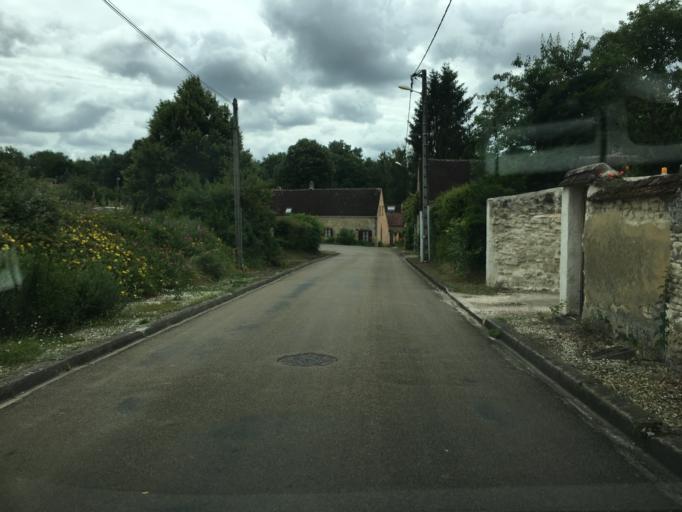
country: FR
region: Bourgogne
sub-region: Departement de l'Yonne
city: Fleury-la-Vallee
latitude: 47.8831
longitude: 3.4177
